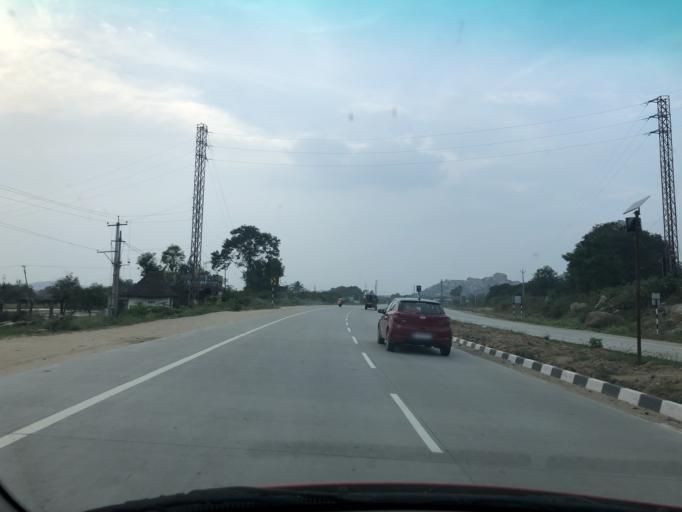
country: IN
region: Andhra Pradesh
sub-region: Chittoor
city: Chittoor
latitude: 13.1959
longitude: 79.0037
